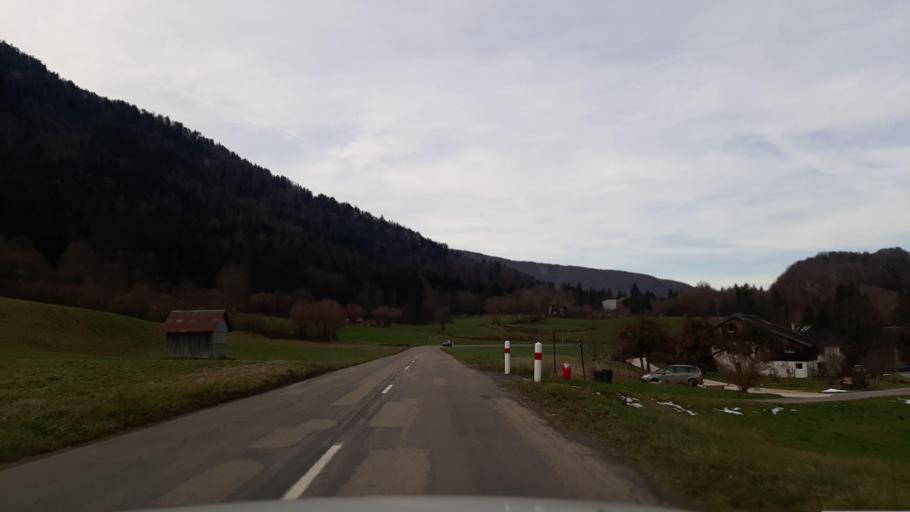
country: FR
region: Rhone-Alpes
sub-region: Departement de la Savoie
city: Gresy-sur-Isere
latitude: 45.6696
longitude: 6.1488
